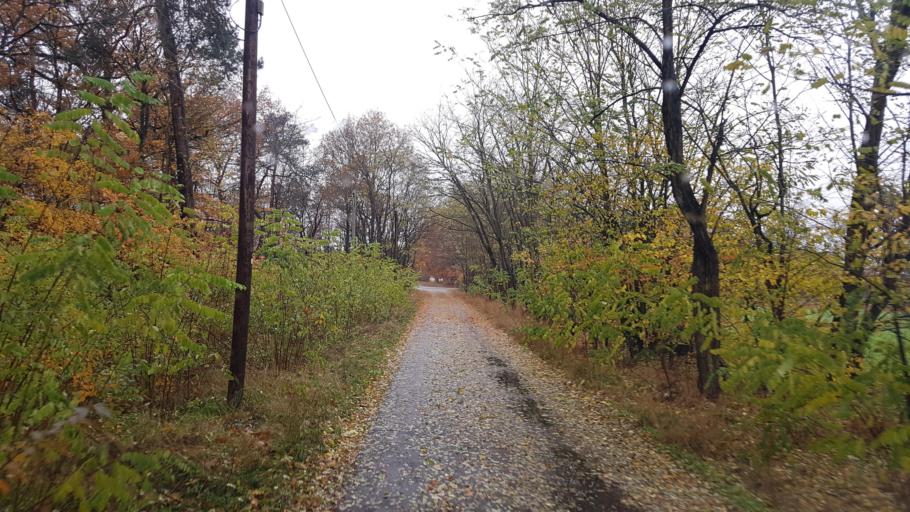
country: DE
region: Brandenburg
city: Altdobern
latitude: 51.6817
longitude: 14.0285
